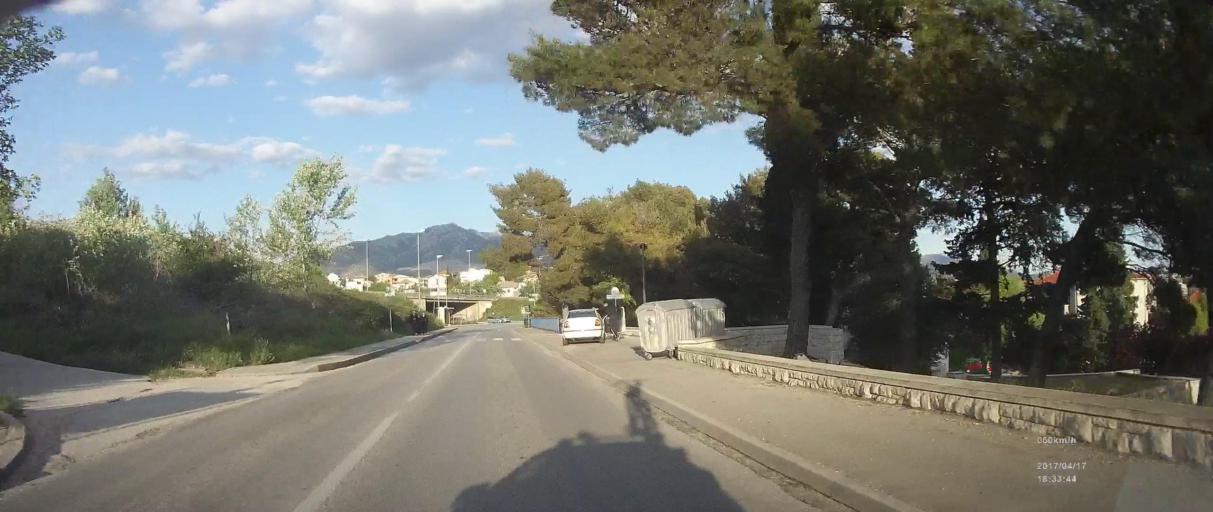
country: HR
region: Splitsko-Dalmatinska
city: Vranjic
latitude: 43.5415
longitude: 16.4634
